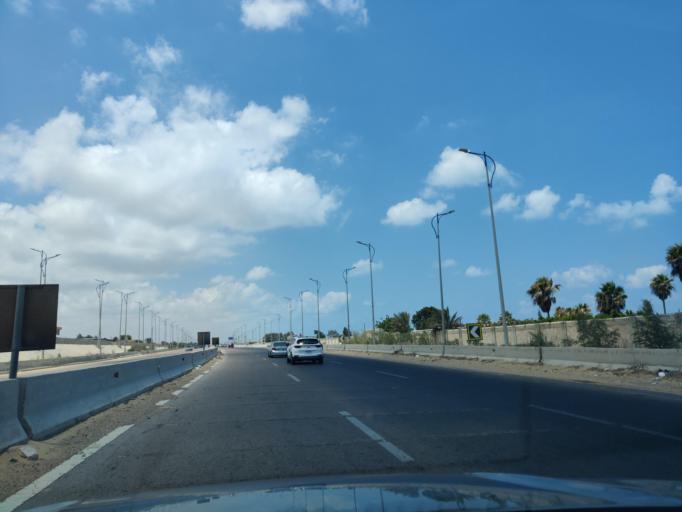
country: EG
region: Alexandria
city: Alexandria
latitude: 30.9456
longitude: 29.5114
